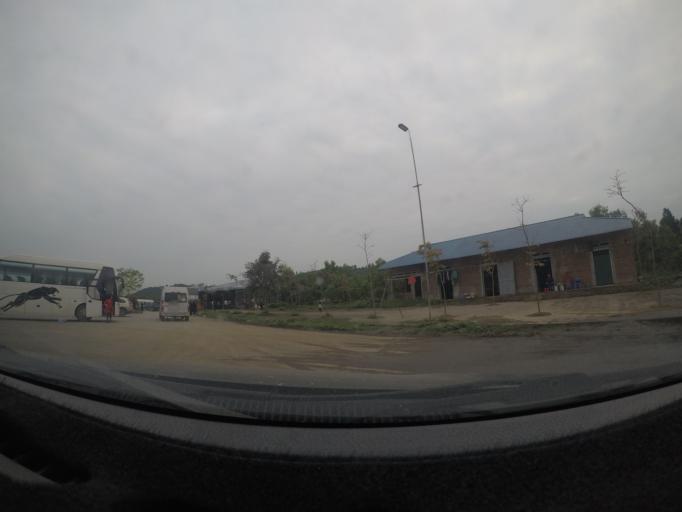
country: VN
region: Yen Bai
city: Yen Bai
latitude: 21.6740
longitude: 104.8779
